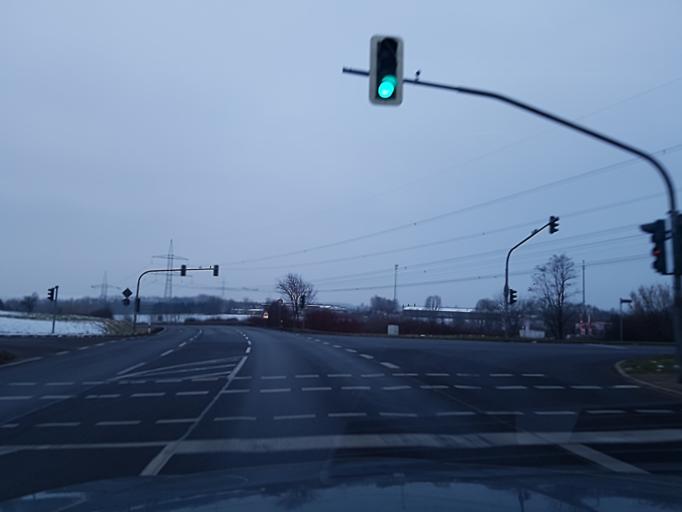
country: DE
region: Saxony
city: Ostrau
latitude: 51.2047
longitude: 13.1537
